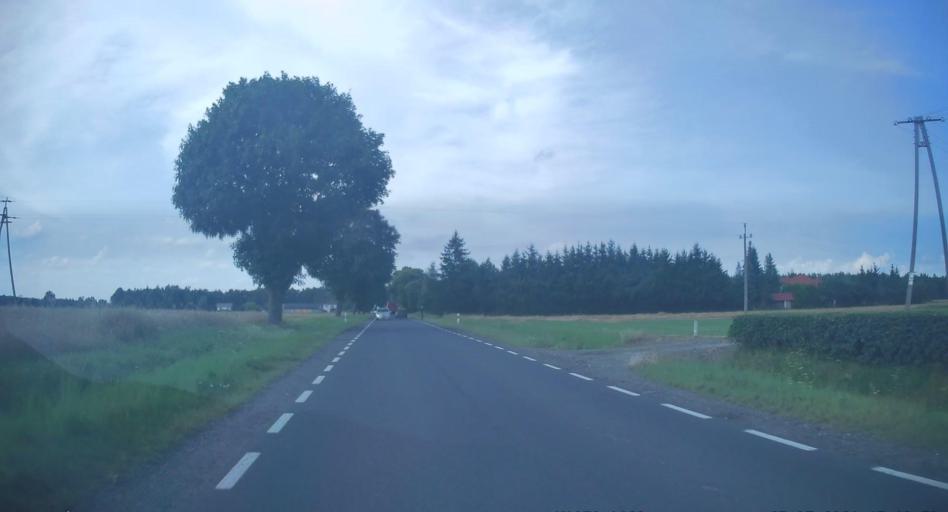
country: PL
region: Lodz Voivodeship
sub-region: Powiat rawski
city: Cieladz
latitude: 51.6792
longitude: 20.2670
